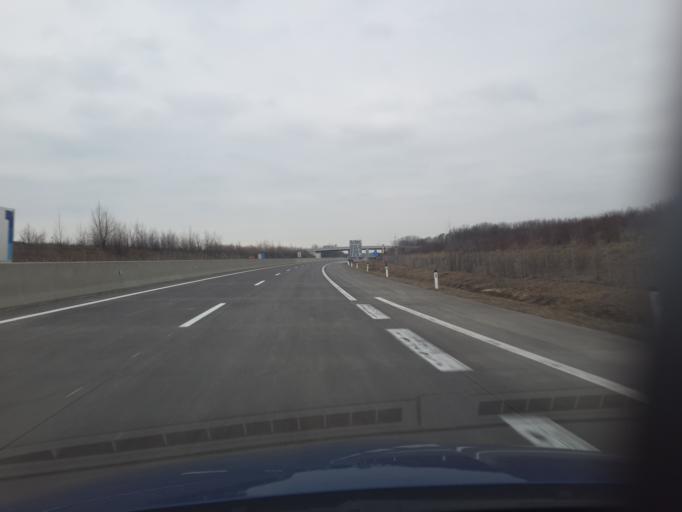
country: AT
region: Burgenland
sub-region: Politischer Bezirk Neusiedl am See
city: Gattendorf
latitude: 48.0350
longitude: 16.9807
